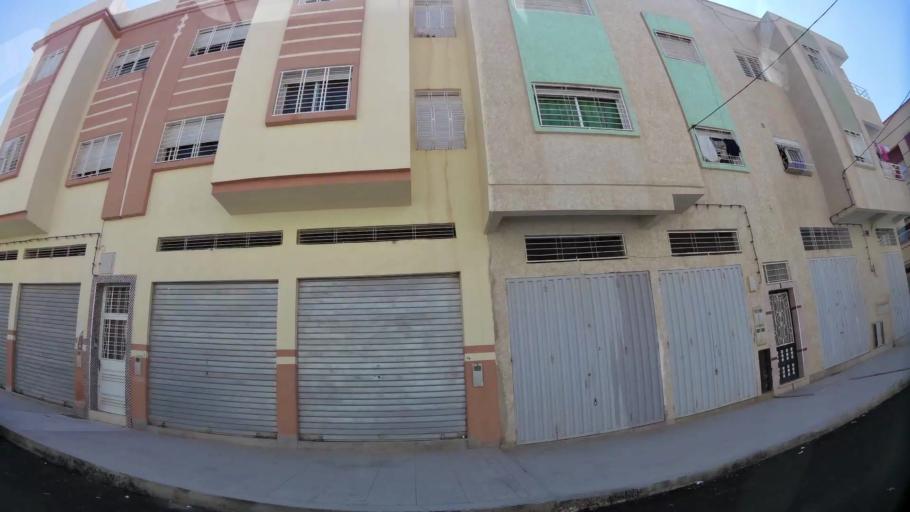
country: MA
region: Fes-Boulemane
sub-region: Fes
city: Fes
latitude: 34.0099
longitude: -5.0355
